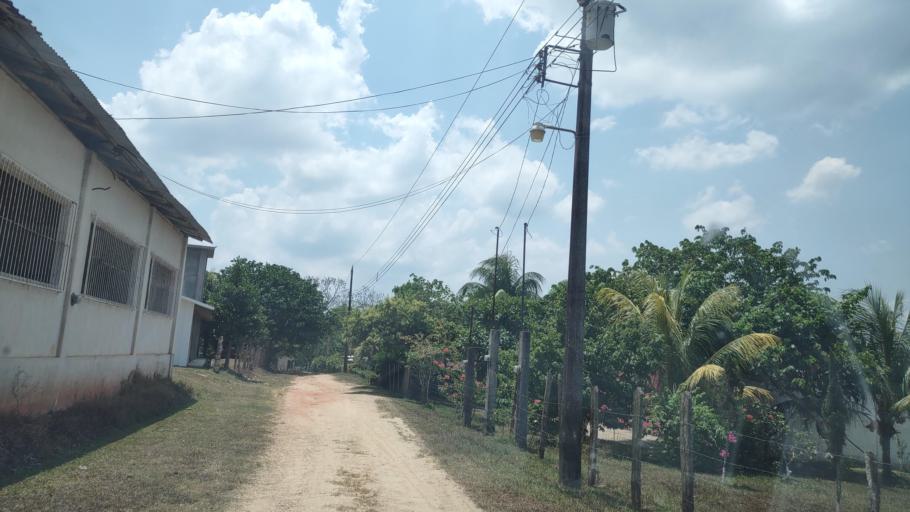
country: MX
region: Veracruz
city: Las Choapas
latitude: 17.9292
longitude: -94.1500
